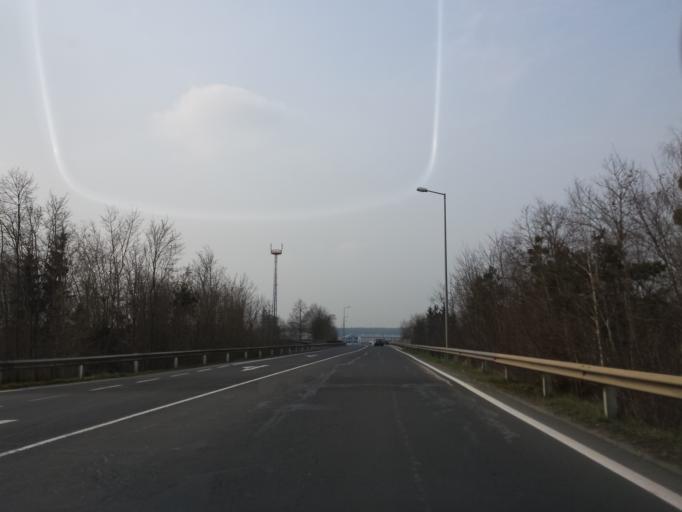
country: AT
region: Styria
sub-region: Politischer Bezirk Hartberg-Fuerstenfeld
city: Ilz
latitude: 47.0802
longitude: 15.9616
